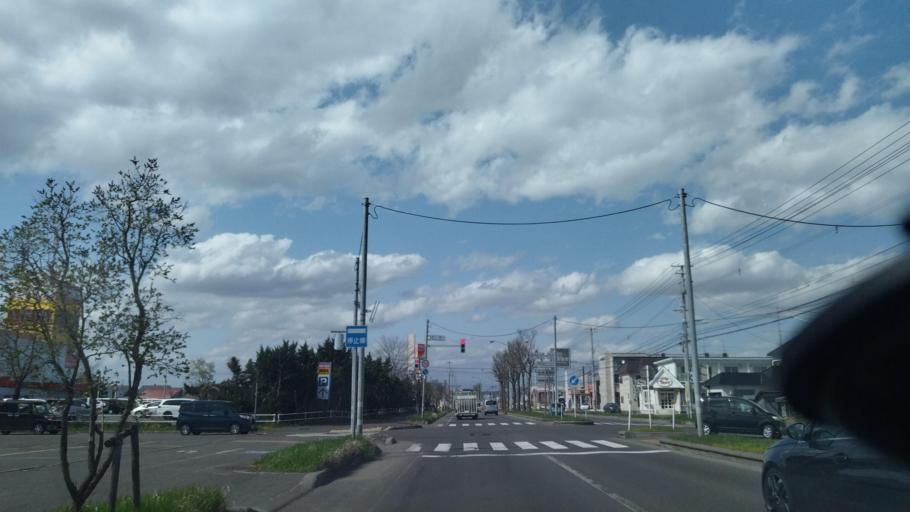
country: JP
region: Hokkaido
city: Obihiro
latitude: 42.9109
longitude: 143.1453
